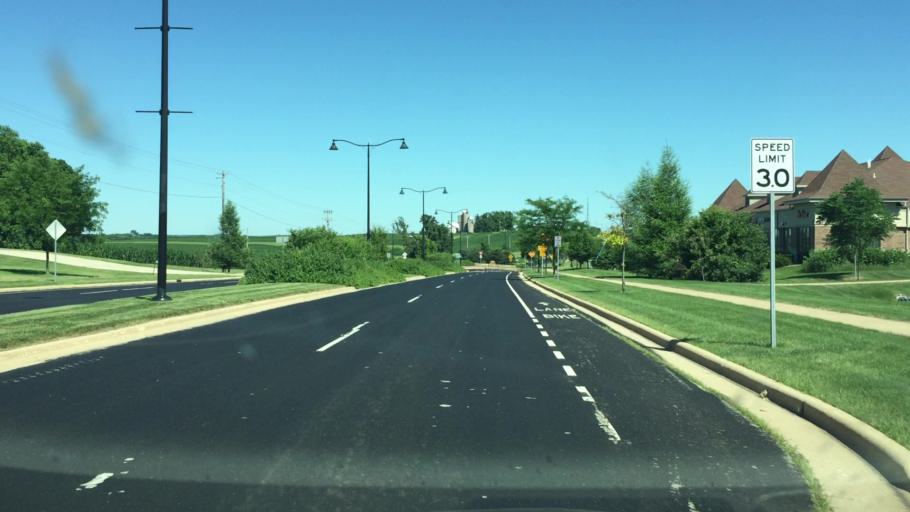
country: US
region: Wisconsin
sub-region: Dane County
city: Mount Horeb
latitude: 43.0096
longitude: -89.7132
